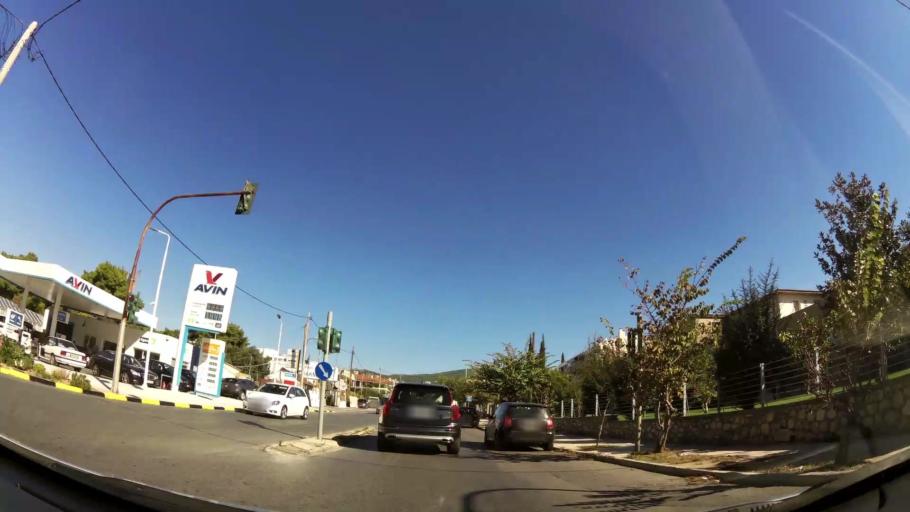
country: GR
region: Attica
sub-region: Nomarchia Athinas
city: Kifisia
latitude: 38.0874
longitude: 23.8096
